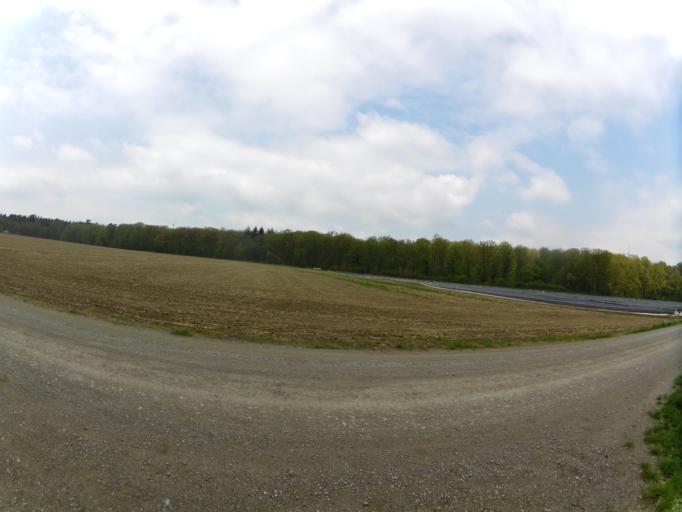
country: DE
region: Bavaria
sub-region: Regierungsbezirk Unterfranken
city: Sommerhausen
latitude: 49.7028
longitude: 10.0610
